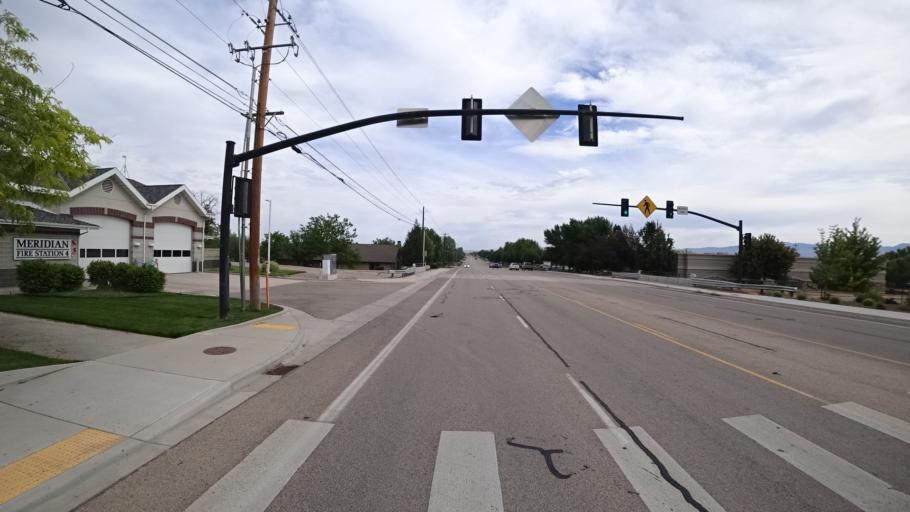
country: US
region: Idaho
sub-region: Ada County
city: Meridian
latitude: 43.5823
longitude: -116.3546
